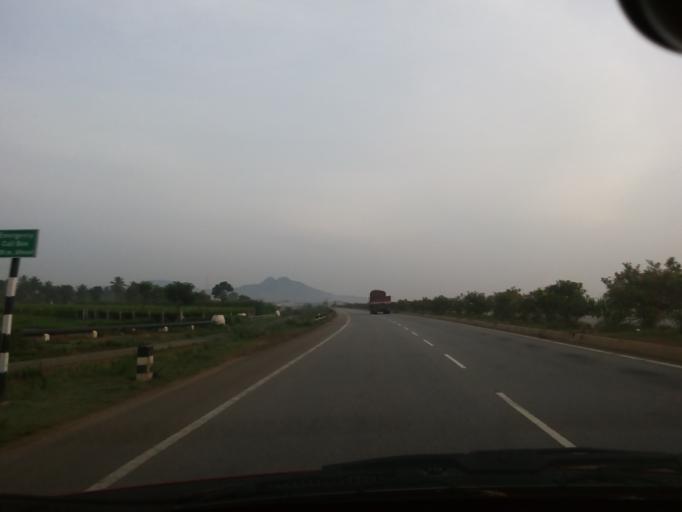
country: IN
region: Karnataka
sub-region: Chikkaballapur
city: Chik Ballapur
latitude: 13.4246
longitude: 77.7441
